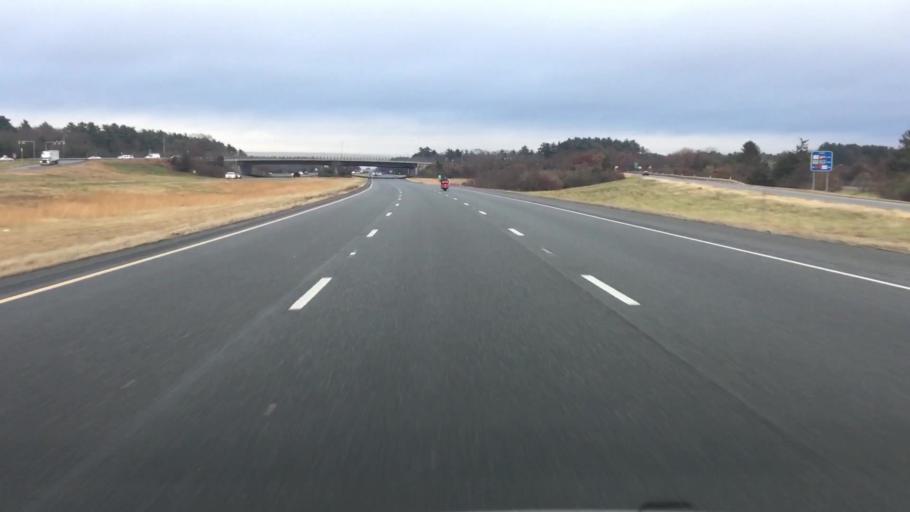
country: US
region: Massachusetts
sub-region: Bristol County
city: Raynham
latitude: 41.9620
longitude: -71.1285
